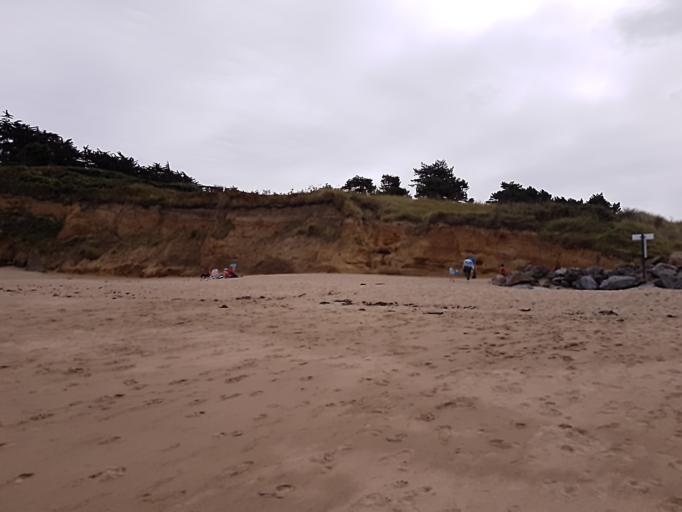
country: FR
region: Brittany
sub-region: Departement des Cotes-d'Armor
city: Saint-Cast-le-Guildo
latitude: 48.6437
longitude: -2.2571
